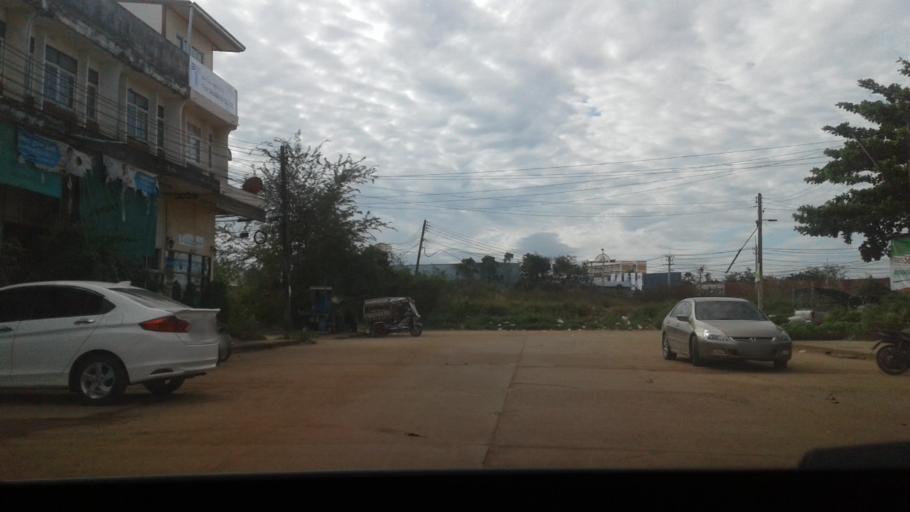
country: TH
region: Changwat Udon Thani
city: Udon Thani
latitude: 17.4328
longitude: 102.7904
